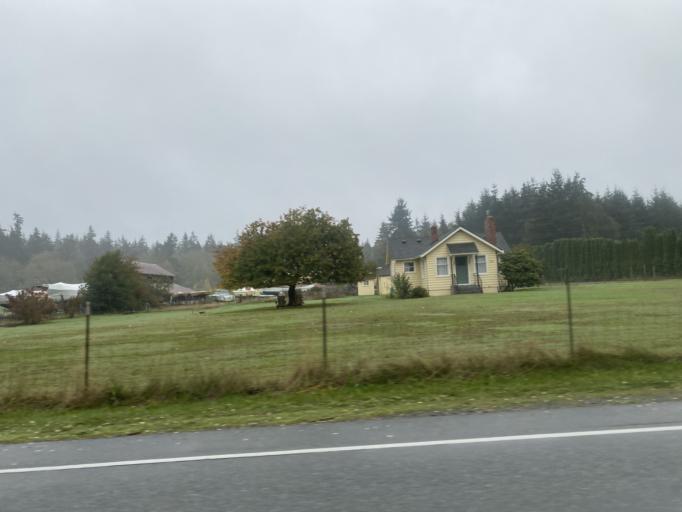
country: US
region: Washington
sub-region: Island County
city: Freeland
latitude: 48.0371
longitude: -122.5069
